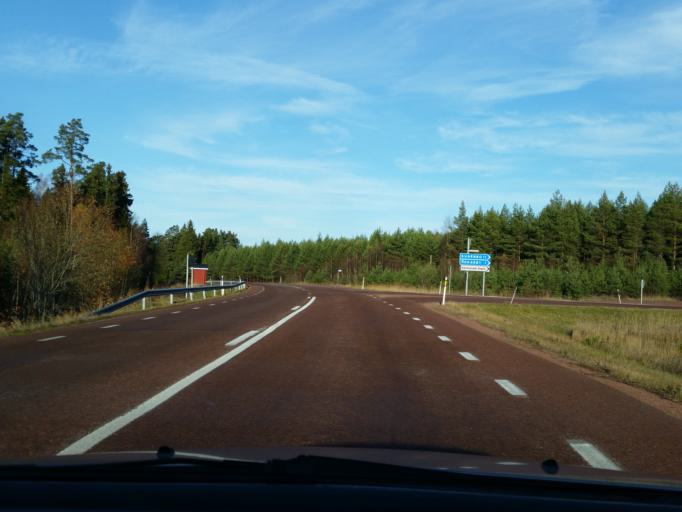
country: AX
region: Alands landsbygd
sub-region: Finstroem
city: Finstroem
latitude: 60.3044
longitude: 19.9523
